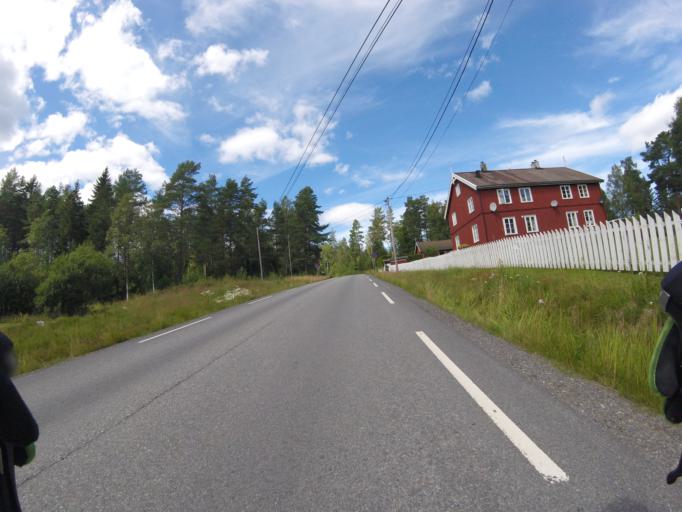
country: NO
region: Akershus
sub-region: Lorenskog
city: Kjenn
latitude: 59.8919
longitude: 10.9776
